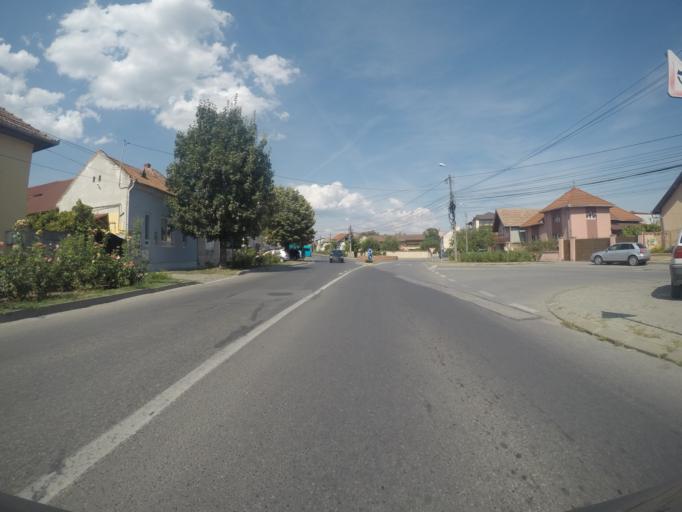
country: RO
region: Alba
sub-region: Municipiul Alba Iulia
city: Alba Iulia
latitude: 46.0751
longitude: 23.5768
